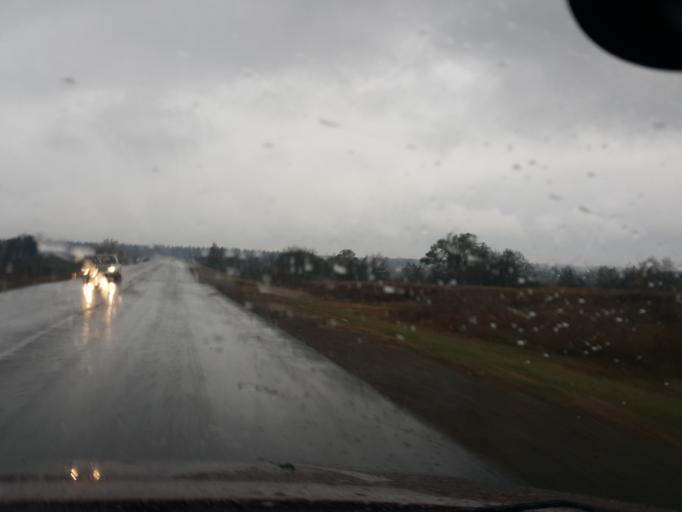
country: RU
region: Tambov
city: Kotovsk
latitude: 52.5322
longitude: 41.4883
